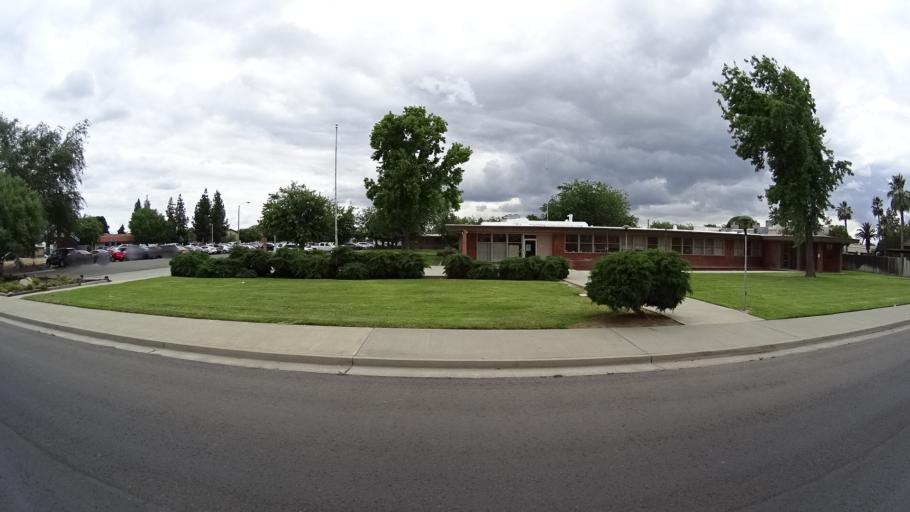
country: US
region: California
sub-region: Kings County
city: Hanford
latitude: 36.3280
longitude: -119.6647
